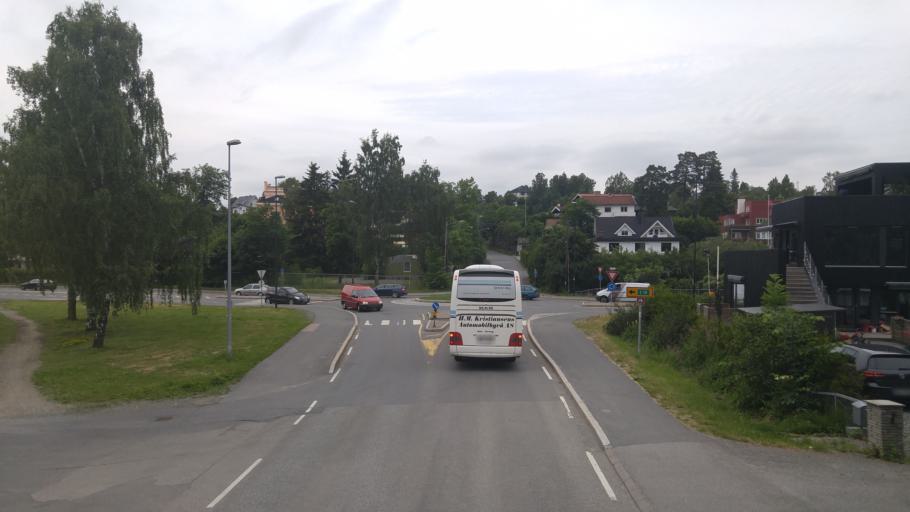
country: NO
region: Akershus
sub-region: Baerum
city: Sandvika
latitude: 59.8927
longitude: 10.5558
